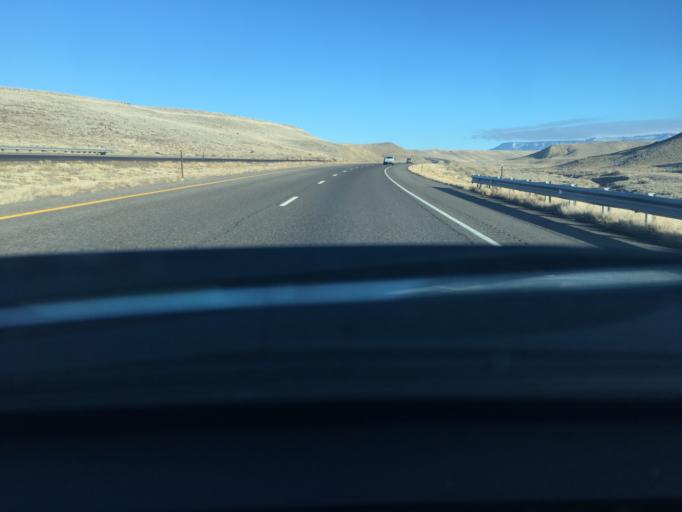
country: US
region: Colorado
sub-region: Delta County
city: Delta
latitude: 38.8299
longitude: -108.2980
